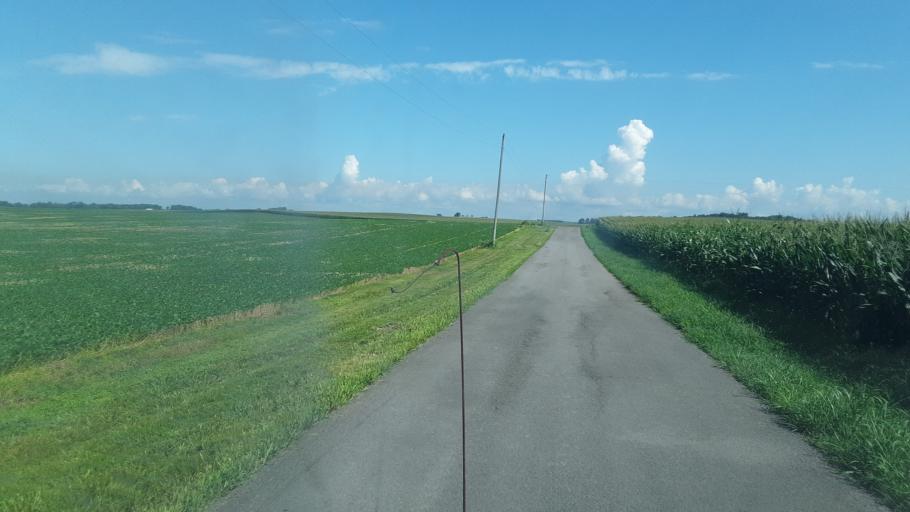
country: US
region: Kentucky
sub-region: Todd County
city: Elkton
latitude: 36.7589
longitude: -87.2275
